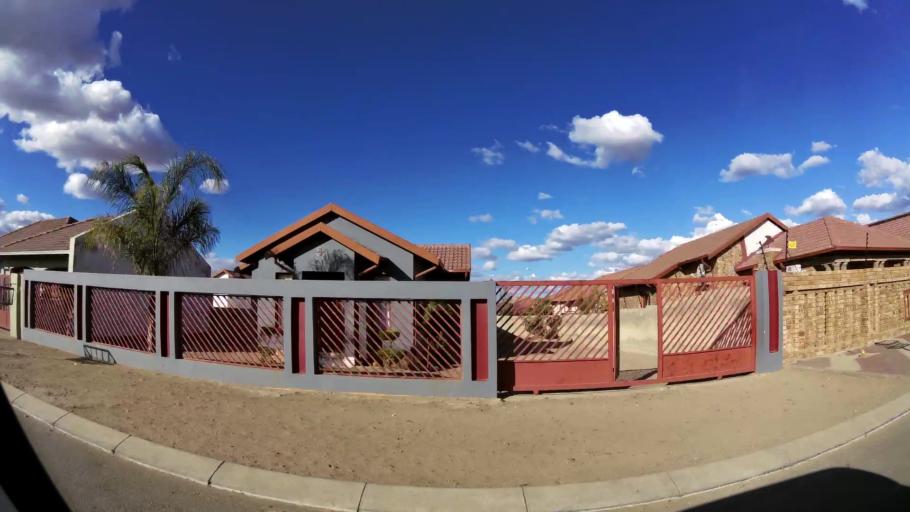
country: ZA
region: Limpopo
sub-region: Capricorn District Municipality
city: Polokwane
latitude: -23.9403
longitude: 29.4424
